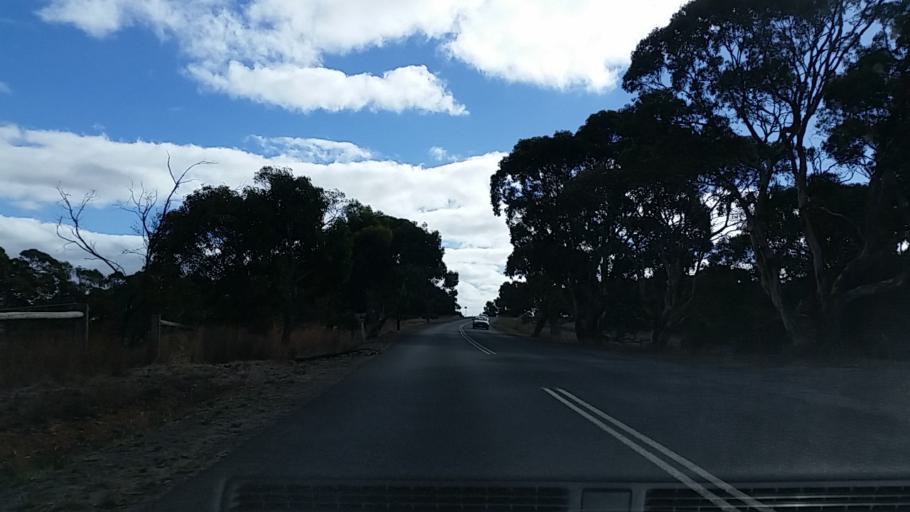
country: AU
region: South Australia
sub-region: Yankalilla
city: Normanville
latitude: -35.4087
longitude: 138.4060
